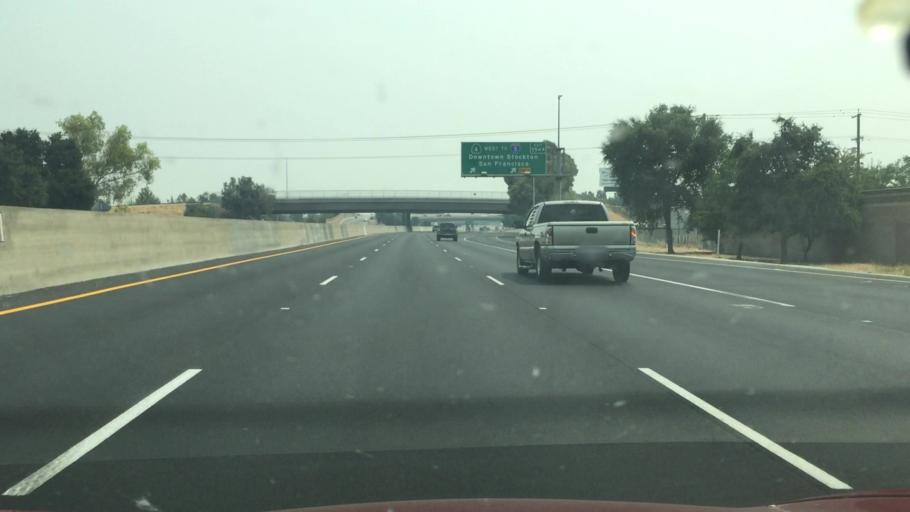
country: US
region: California
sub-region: San Joaquin County
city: Garden Acres
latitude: 37.9666
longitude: -121.2443
